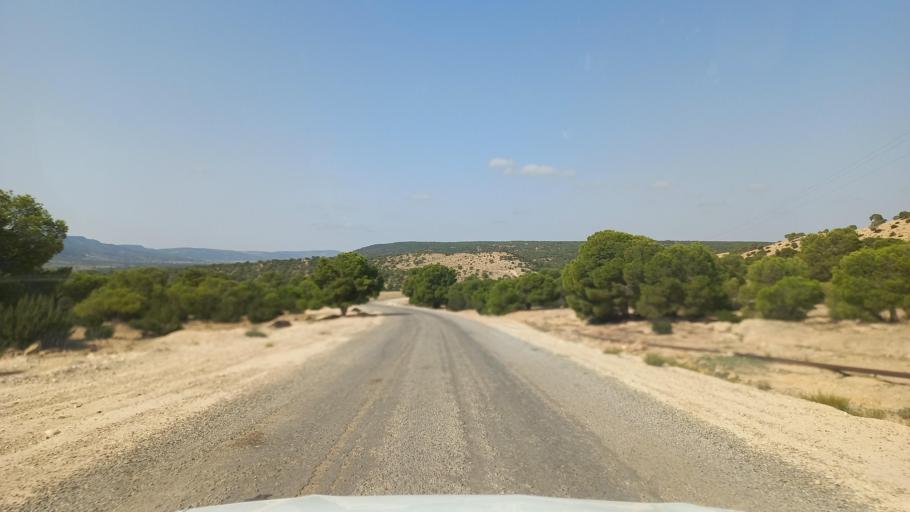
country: TN
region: Al Qasrayn
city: Sbiba
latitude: 35.3980
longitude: 8.9557
